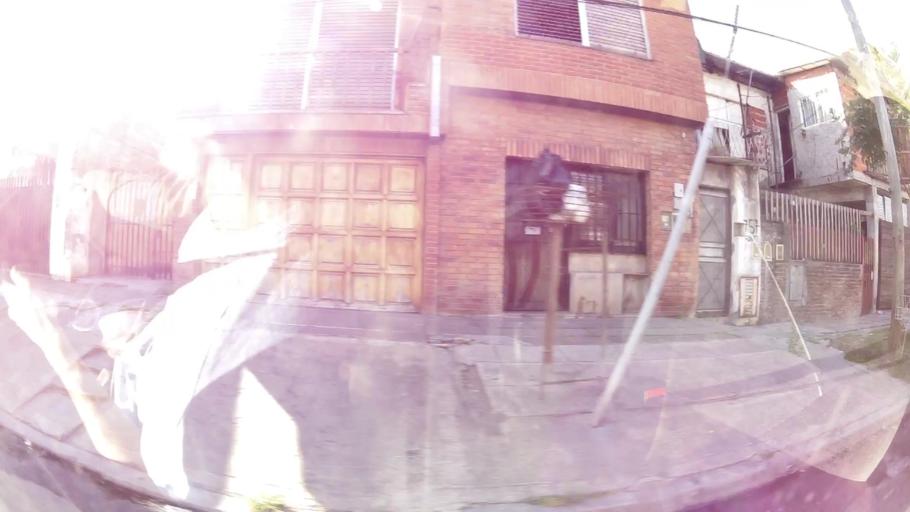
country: AR
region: Buenos Aires
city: Hurlingham
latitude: -34.5580
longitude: -58.6107
